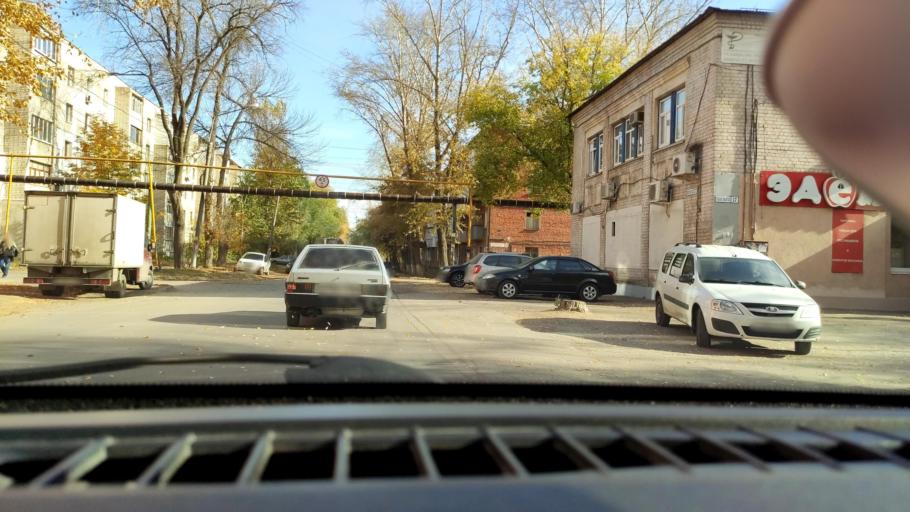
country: RU
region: Samara
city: Petra-Dubrava
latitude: 53.2980
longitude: 50.2885
